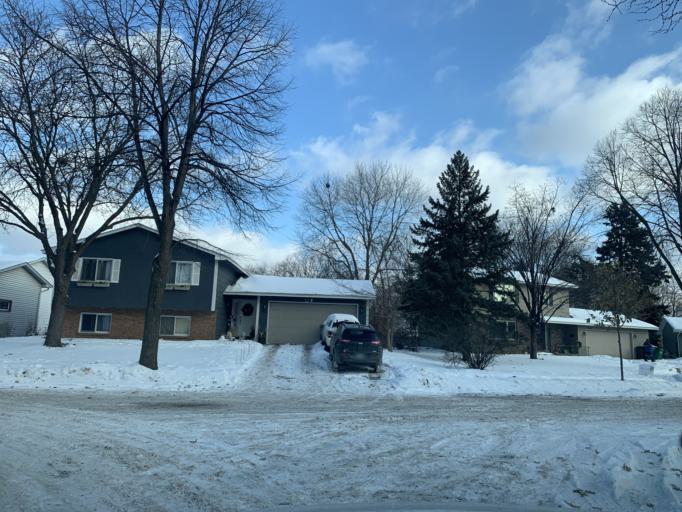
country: US
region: Minnesota
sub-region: Hennepin County
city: Minneapolis
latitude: 44.9960
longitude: -93.2866
